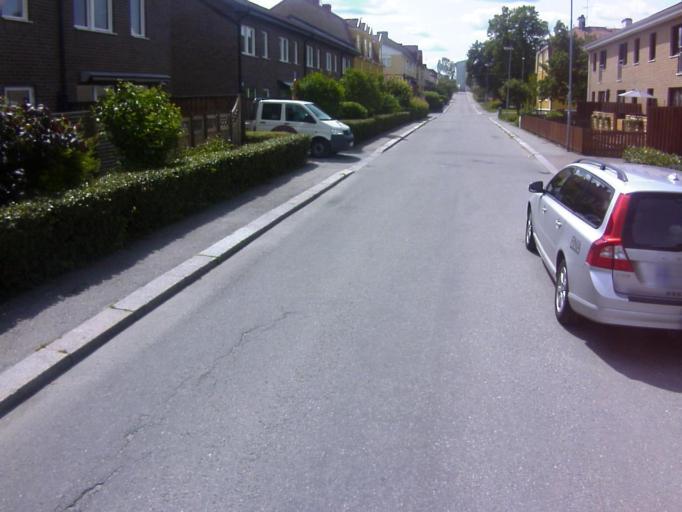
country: SE
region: Soedermanland
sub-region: Eskilstuna Kommun
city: Eskilstuna
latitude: 59.3649
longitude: 16.5225
